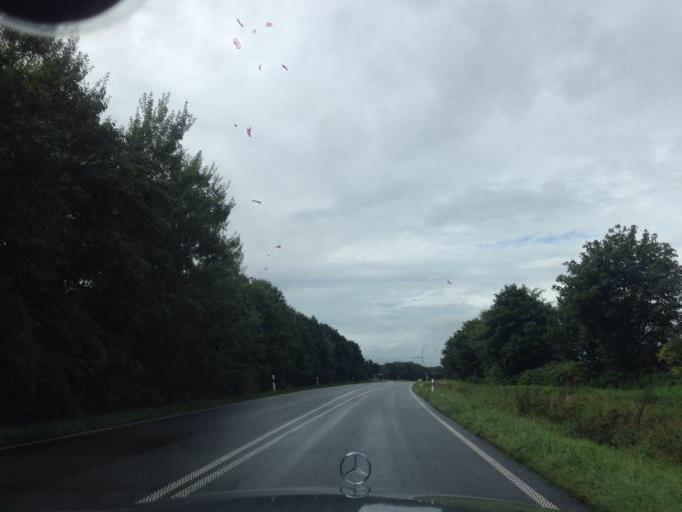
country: DE
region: Schleswig-Holstein
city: Horup
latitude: 54.7479
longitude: 9.1073
